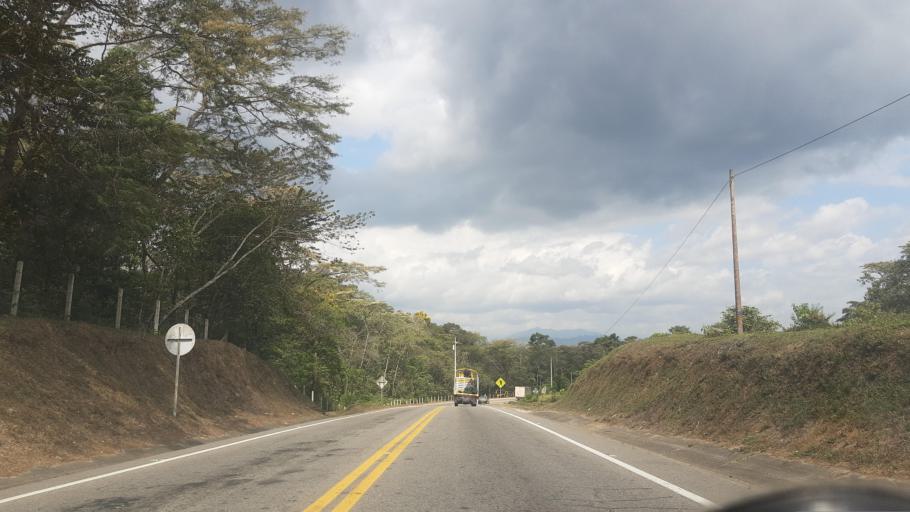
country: CO
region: Casanare
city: Tauramena
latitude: 5.0049
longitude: -72.6896
